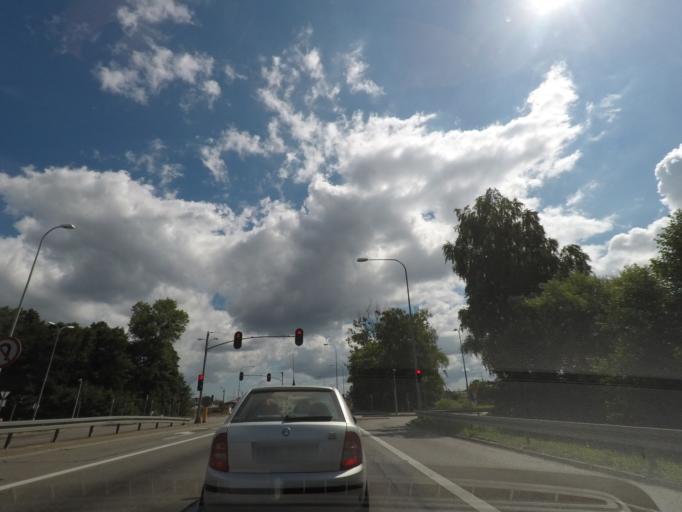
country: PL
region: Pomeranian Voivodeship
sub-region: Powiat wejherowski
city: Wejherowo
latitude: 54.6081
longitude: 18.2116
